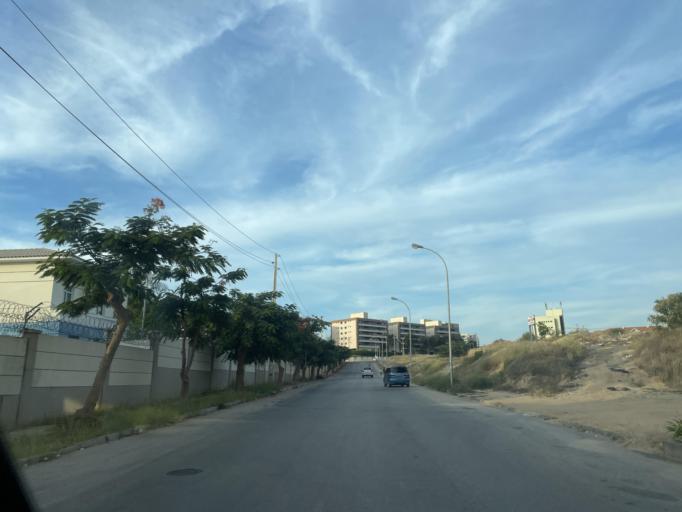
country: AO
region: Luanda
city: Luanda
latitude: -8.9295
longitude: 13.1872
